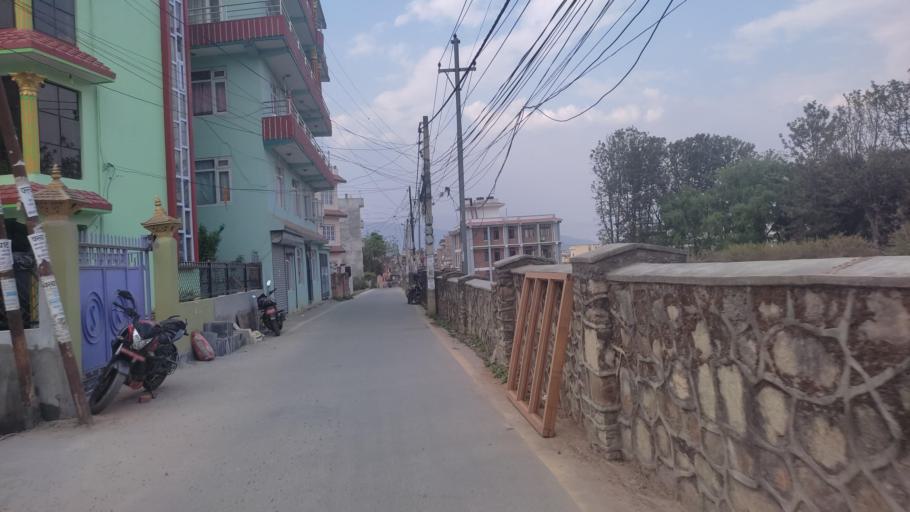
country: NP
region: Central Region
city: Kirtipur
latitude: 27.6828
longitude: 85.2816
